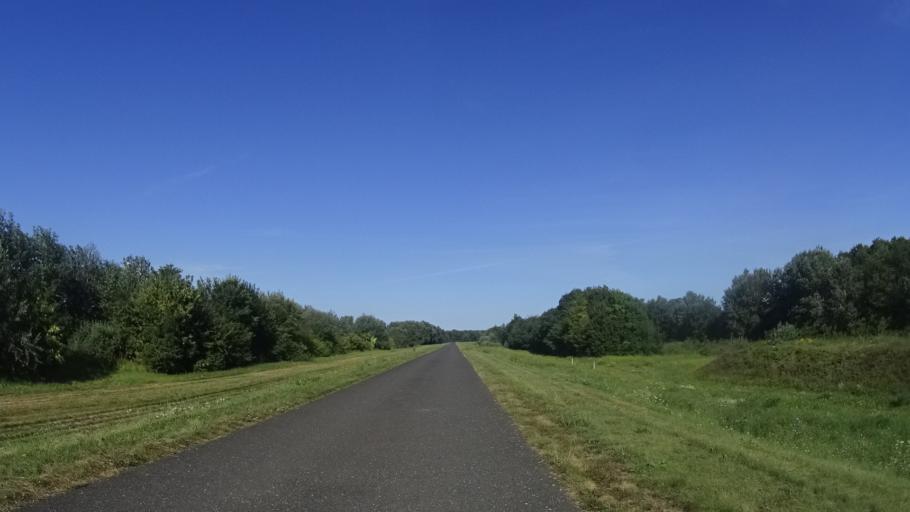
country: HU
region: Gyor-Moson-Sopron
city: Rajka
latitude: 48.0622
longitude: 17.1888
